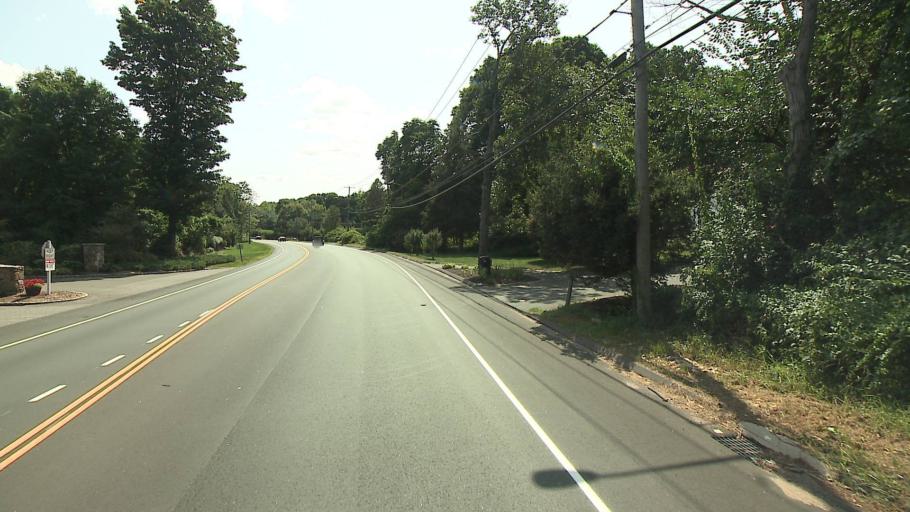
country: US
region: Connecticut
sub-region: Fairfield County
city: Trumbull
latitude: 41.2908
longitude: -73.2425
